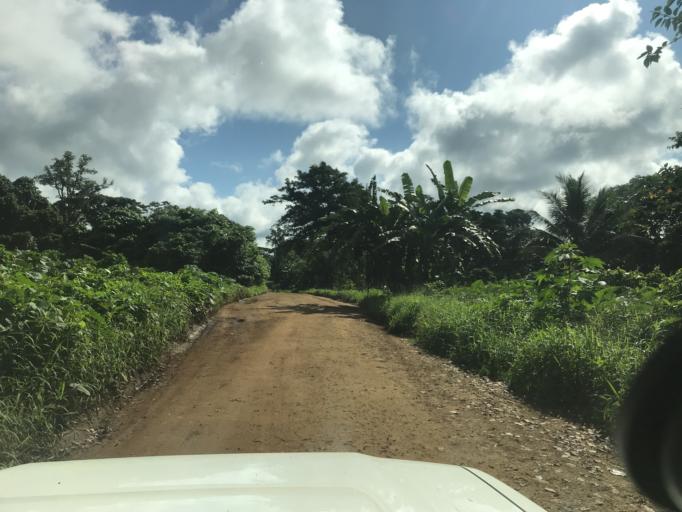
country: VU
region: Sanma
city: Luganville
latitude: -15.4841
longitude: 167.0895
